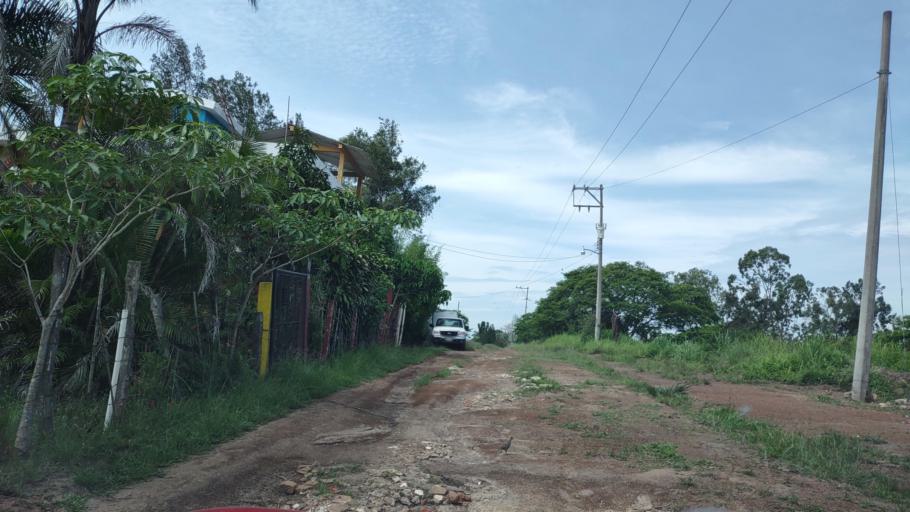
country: MX
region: Veracruz
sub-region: Emiliano Zapata
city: Dos Rios
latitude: 19.4725
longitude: -96.8265
